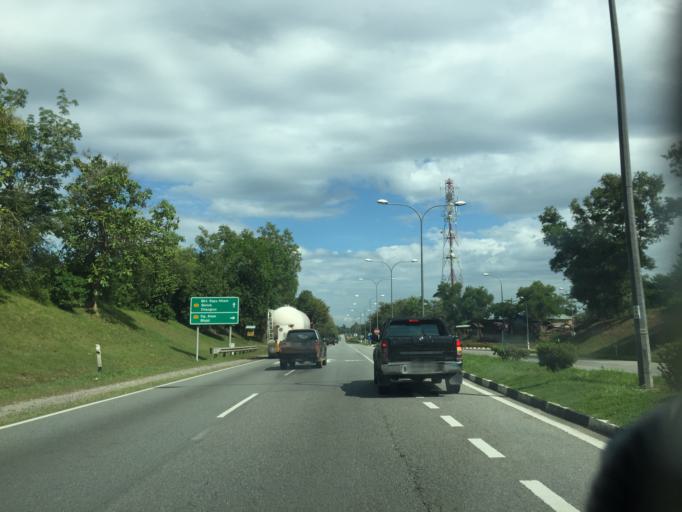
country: MY
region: Kedah
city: Jitra
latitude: 6.3288
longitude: 100.4204
